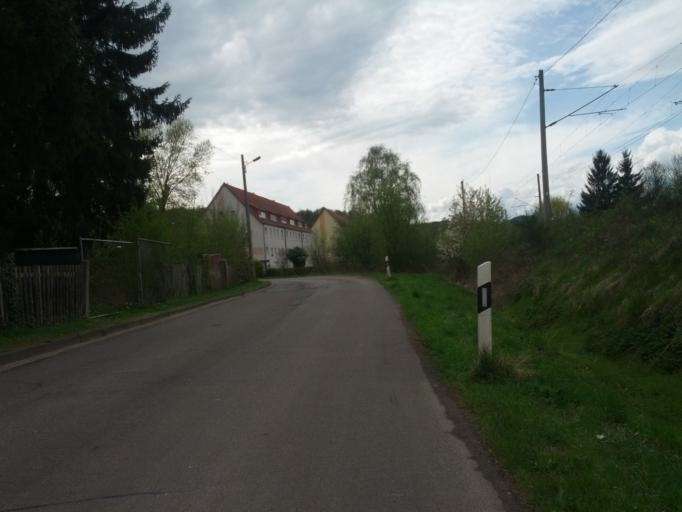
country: DE
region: Thuringia
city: Eisenach
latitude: 50.9781
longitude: 10.2906
